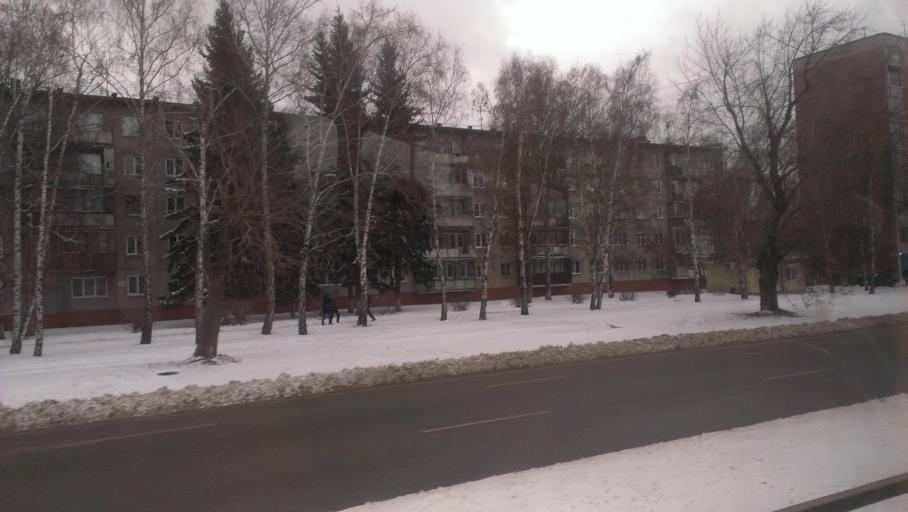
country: RU
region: Altai Krai
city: Novosilikatnyy
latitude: 53.3692
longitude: 83.6772
